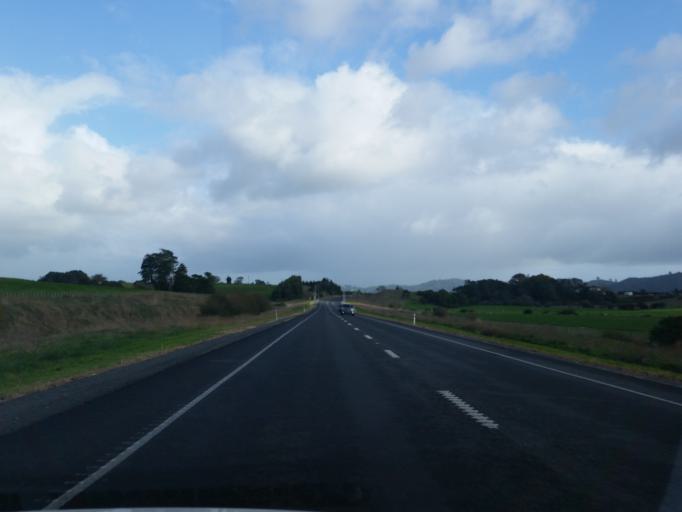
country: NZ
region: Auckland
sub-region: Auckland
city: Pukekohe East
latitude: -37.2208
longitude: 175.1288
